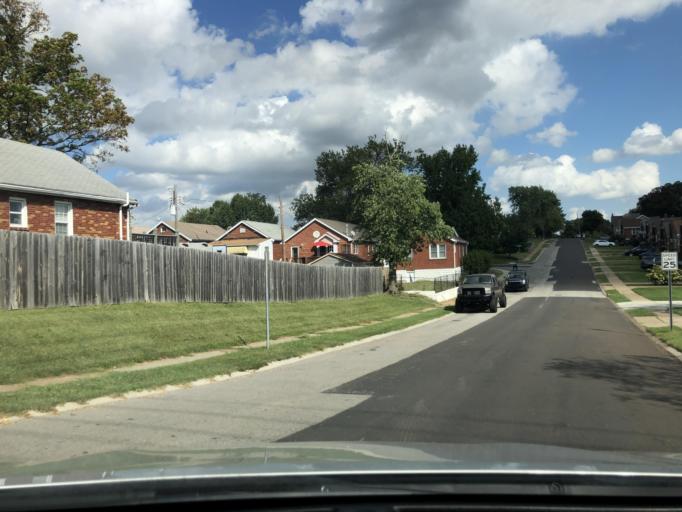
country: US
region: Missouri
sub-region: Saint Louis County
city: Affton
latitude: 38.5485
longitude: -90.3232
